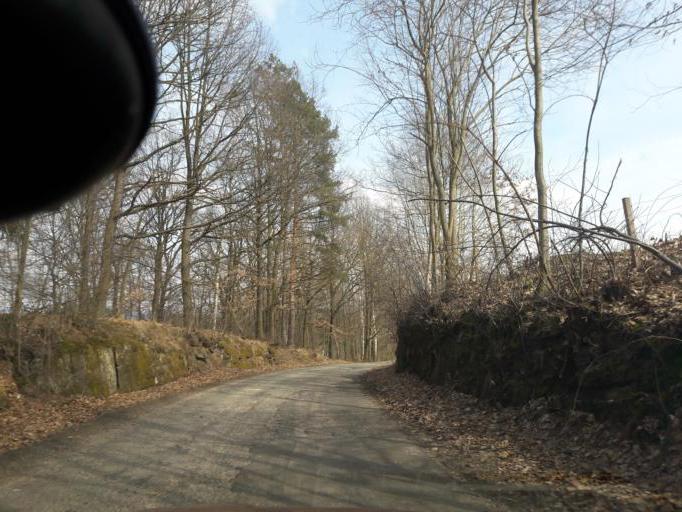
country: CZ
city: Cvikov
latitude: 50.7304
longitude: 14.6244
